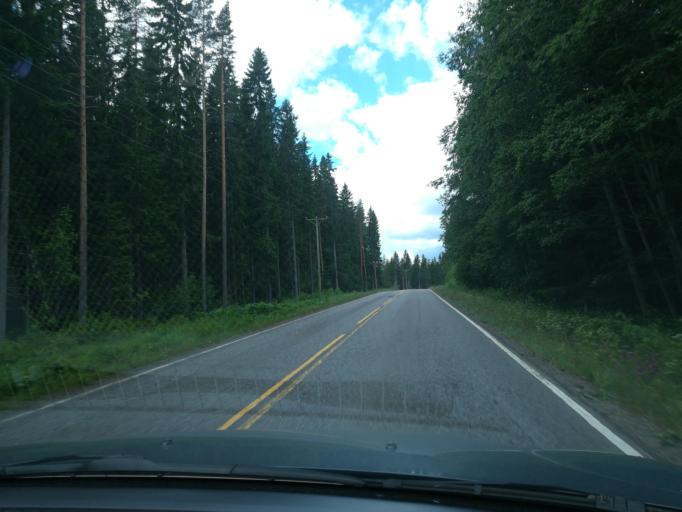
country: FI
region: Southern Savonia
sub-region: Mikkeli
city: Maentyharju
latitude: 61.3574
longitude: 27.0898
